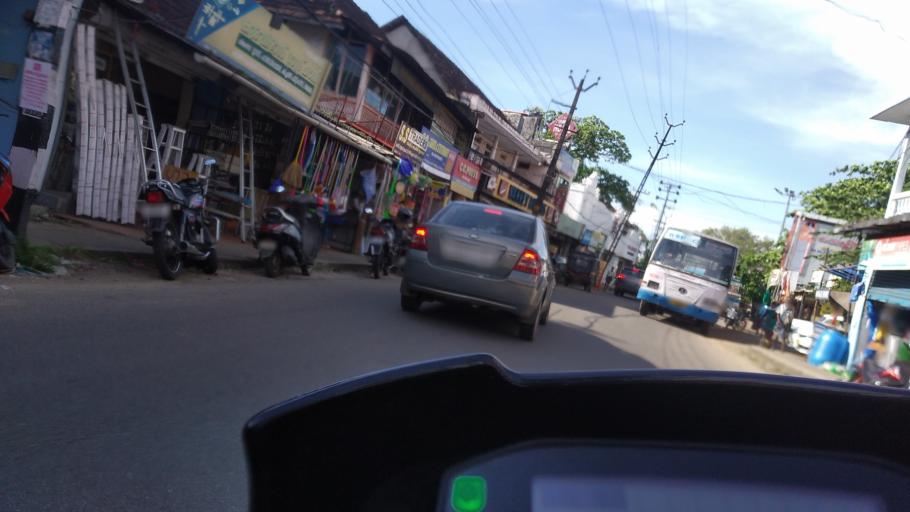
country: IN
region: Kerala
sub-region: Ernakulam
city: Elur
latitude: 10.0466
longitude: 76.2174
